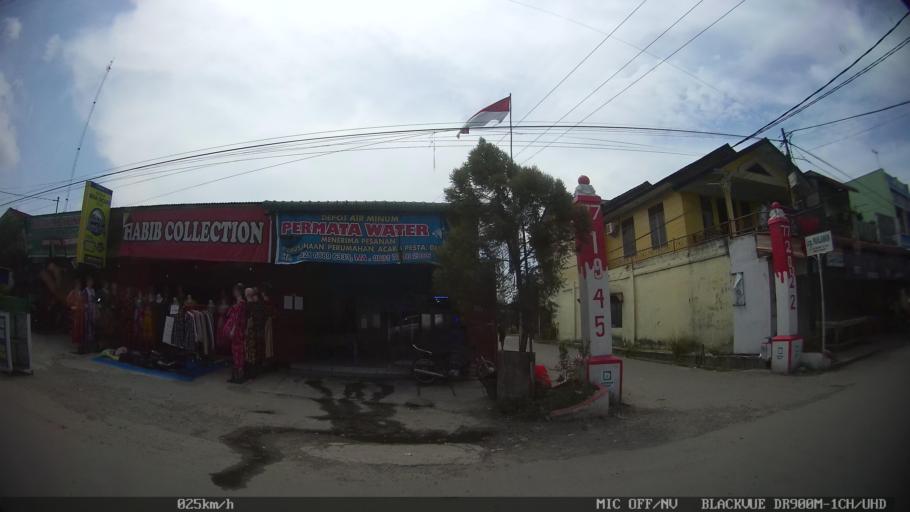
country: ID
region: North Sumatra
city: Labuhan Deli
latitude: 3.6662
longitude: 98.6794
